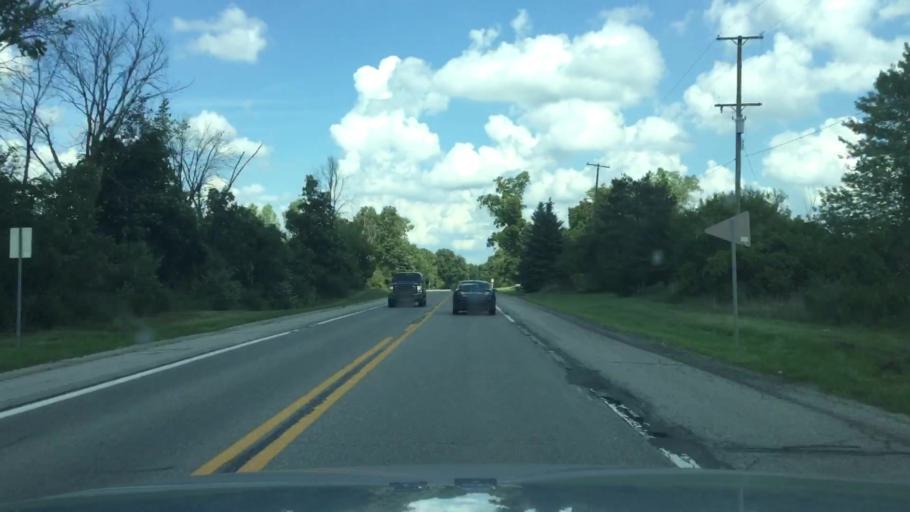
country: US
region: Michigan
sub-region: Lenawee County
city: Clinton
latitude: 42.1100
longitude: -83.8891
